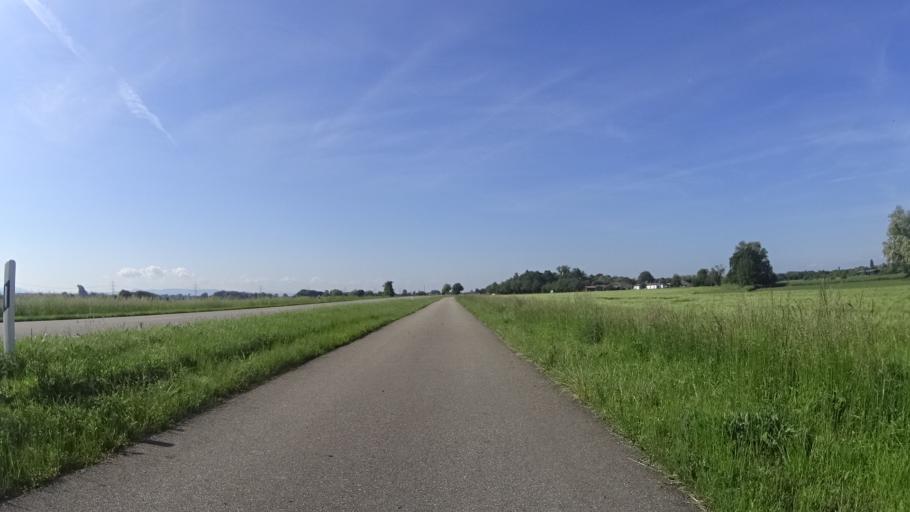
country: DE
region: Baden-Wuerttemberg
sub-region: Freiburg Region
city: Kehl
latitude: 48.5427
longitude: 7.8341
